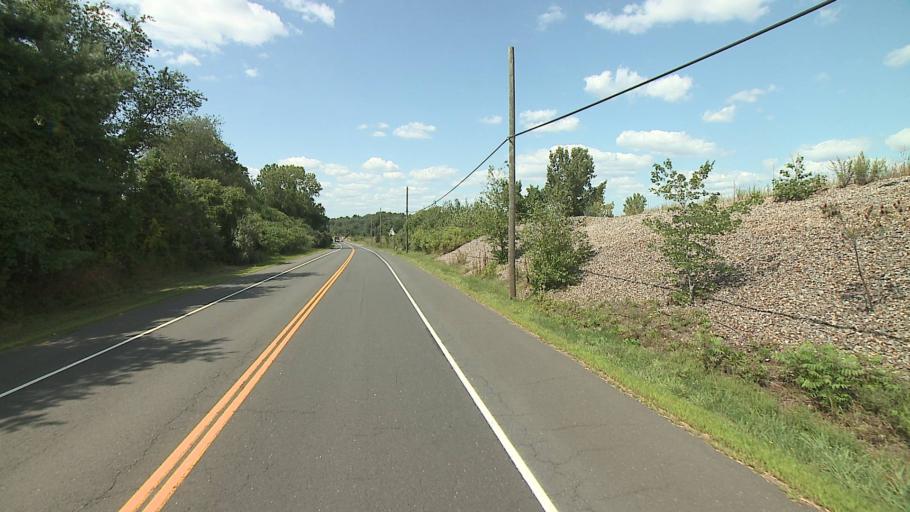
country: US
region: Connecticut
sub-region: Tolland County
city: Ellington
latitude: 41.9221
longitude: -72.5024
